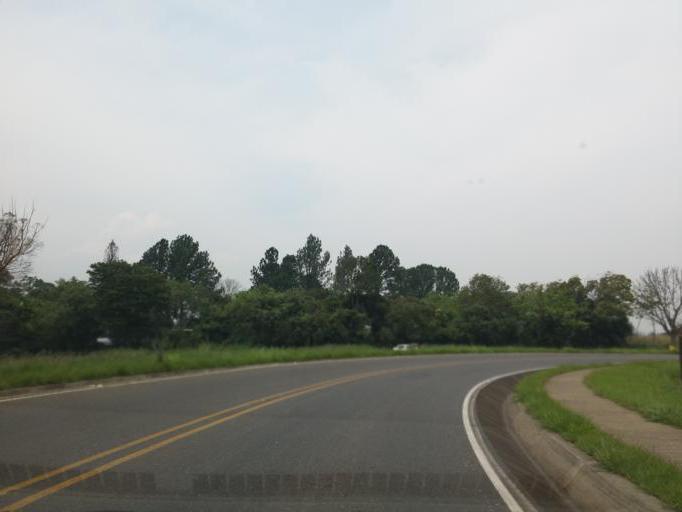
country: CR
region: Heredia
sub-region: Canton de Belen
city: San Antonio
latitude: 9.9967
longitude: -84.1943
